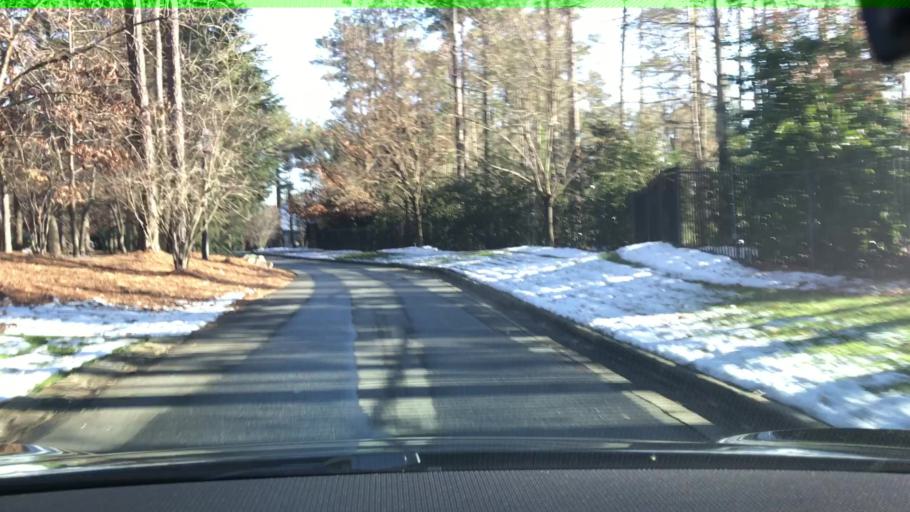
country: US
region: Georgia
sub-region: Gwinnett County
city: Suwanee
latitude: 34.0703
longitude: -84.0928
